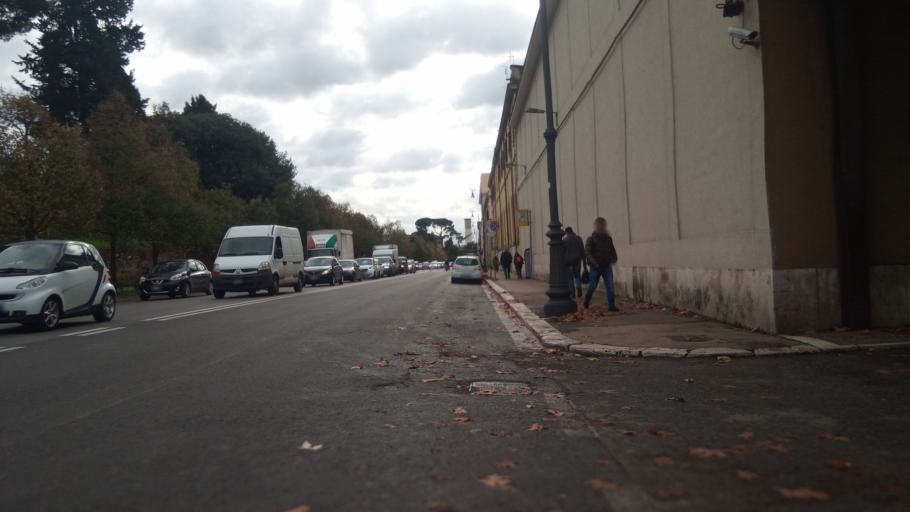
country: IT
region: Latium
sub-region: Citta metropolitana di Roma Capitale
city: Rome
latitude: 41.9019
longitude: 12.5072
